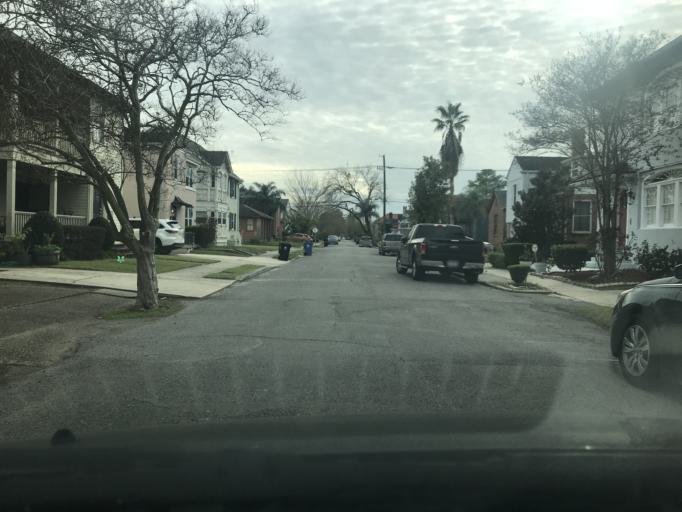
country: US
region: Louisiana
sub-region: Orleans Parish
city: New Orleans
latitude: 29.9554
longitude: -90.1083
